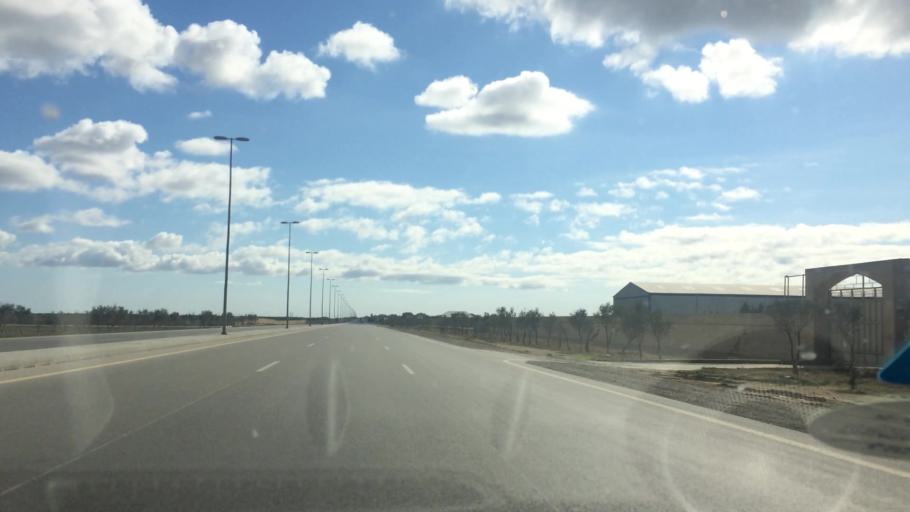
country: AZ
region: Baki
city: Qala
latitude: 40.4560
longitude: 50.1439
